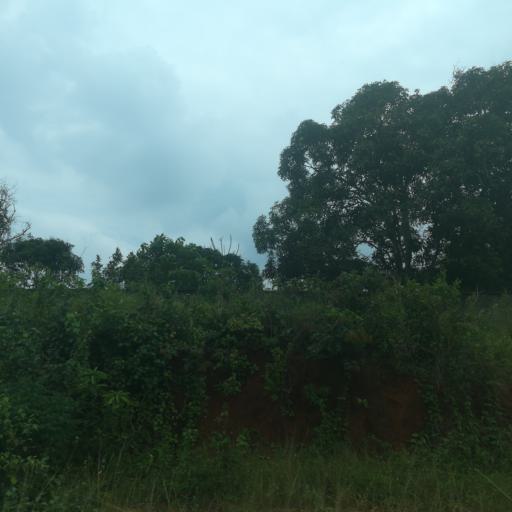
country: NG
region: Lagos
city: Ejirin
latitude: 6.6429
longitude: 3.7247
